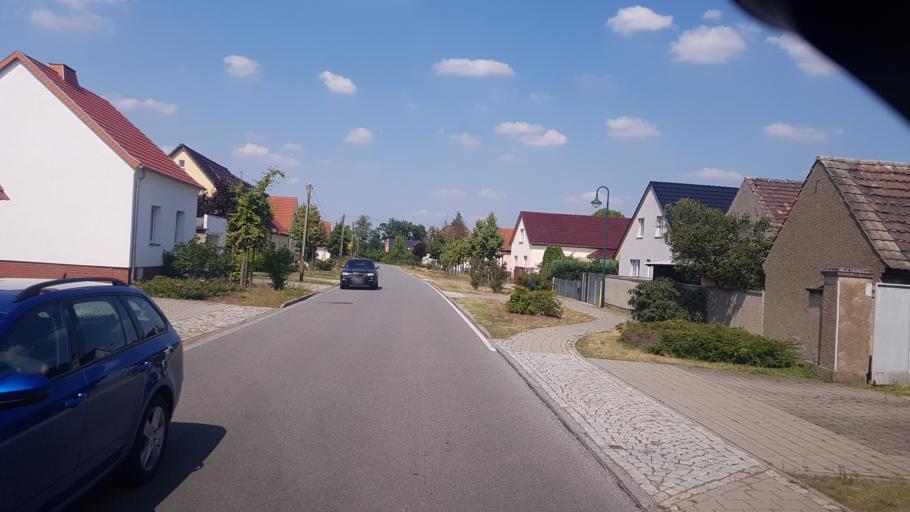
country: DE
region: Brandenburg
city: Cottbus
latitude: 51.6980
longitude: 14.4271
